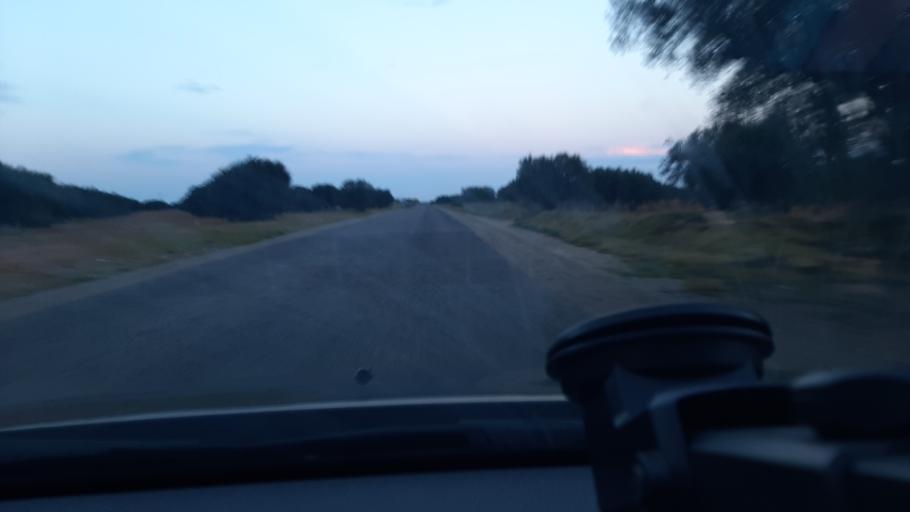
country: TN
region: Al Mahdiyah
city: Shurban
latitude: 34.9890
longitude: 10.3942
